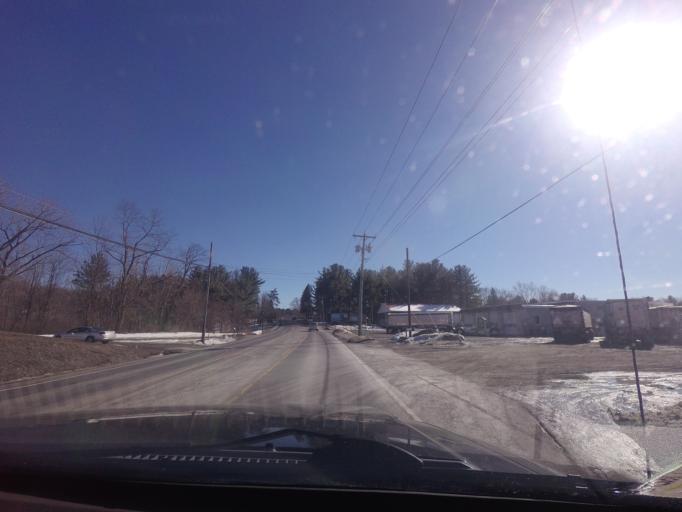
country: US
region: New York
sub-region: Rensselaer County
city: Nassau
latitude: 42.5396
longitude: -73.6640
